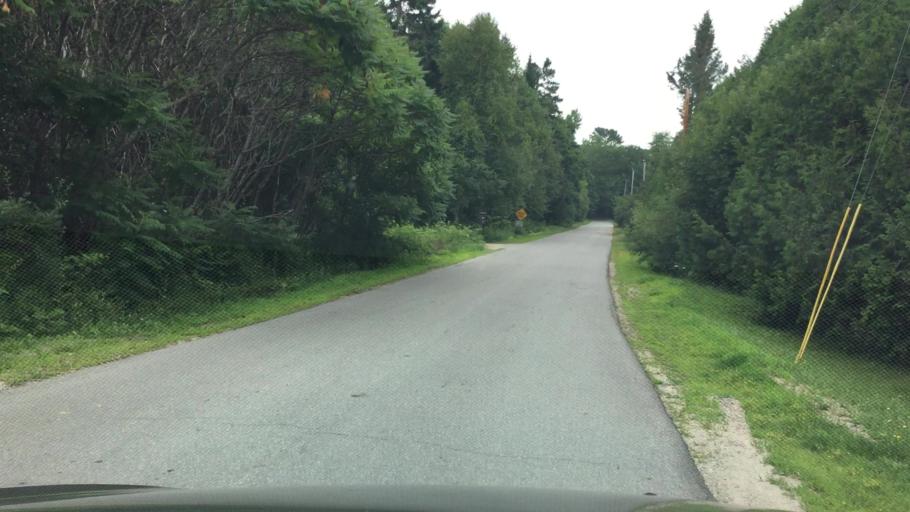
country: US
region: Maine
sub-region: Waldo County
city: Stockton Springs
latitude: 44.5068
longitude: -68.8100
